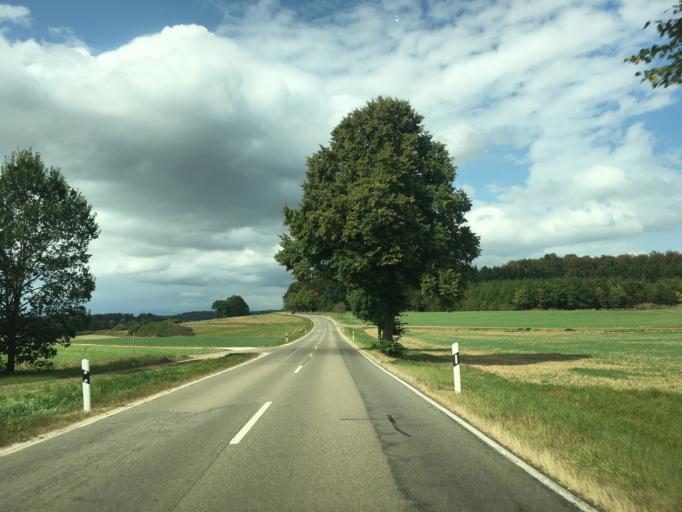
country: DE
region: Baden-Wuerttemberg
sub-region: Tuebingen Region
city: Gomadingen
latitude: 48.3491
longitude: 9.3504
